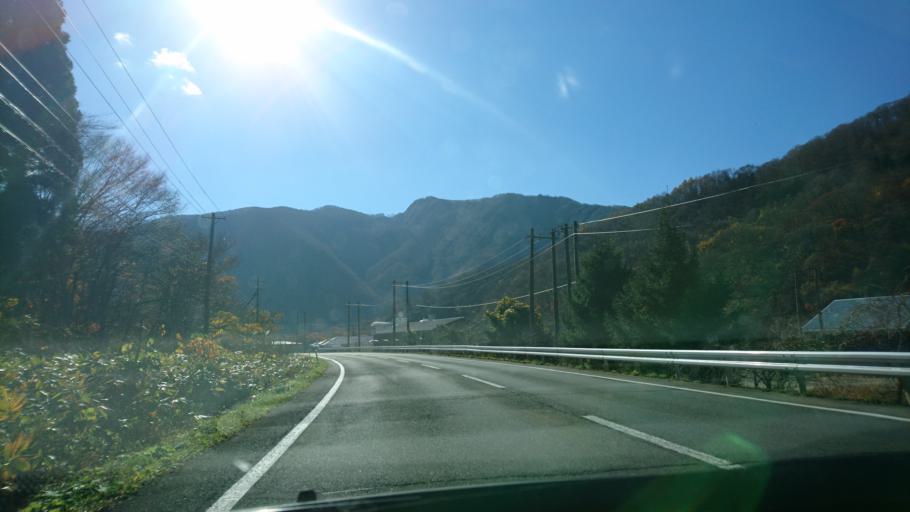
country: JP
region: Iwate
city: Kitakami
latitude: 39.3070
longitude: 140.9019
